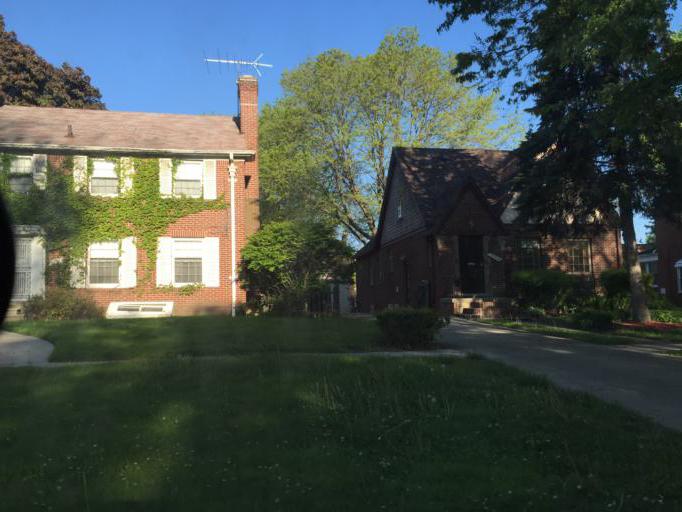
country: US
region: Michigan
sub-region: Wayne County
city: Redford
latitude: 42.4011
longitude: -83.2313
